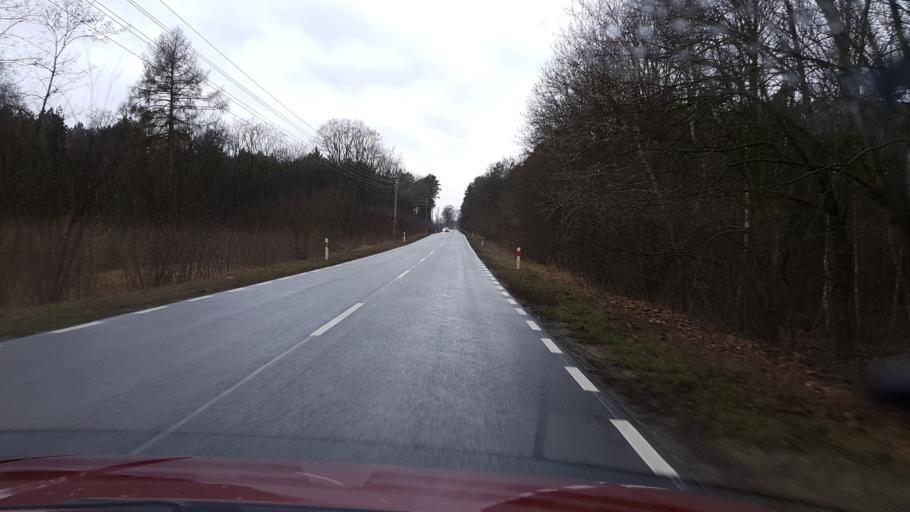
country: PL
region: West Pomeranian Voivodeship
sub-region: Powiat gryfinski
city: Gryfino
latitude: 53.2565
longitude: 14.5321
